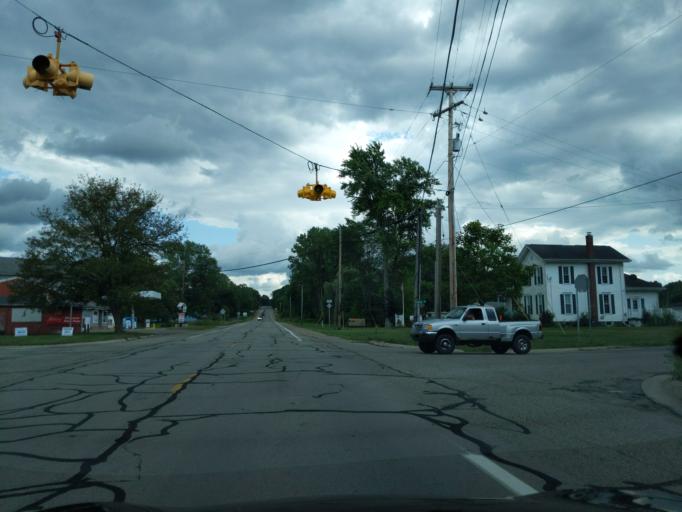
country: US
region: Michigan
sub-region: Ingham County
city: Leslie
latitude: 42.3729
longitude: -84.5443
